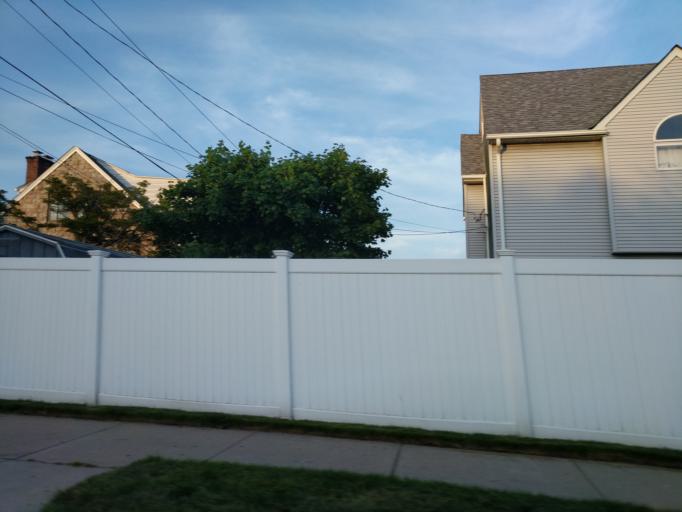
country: US
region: New York
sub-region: Nassau County
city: Long Beach
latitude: 40.5858
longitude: -73.6582
